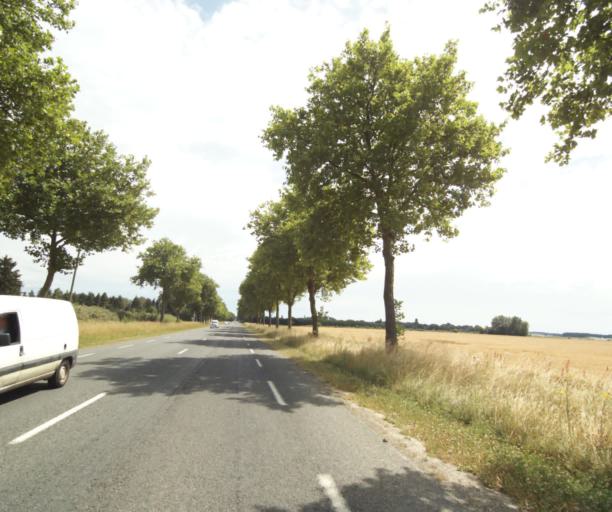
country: FR
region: Ile-de-France
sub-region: Departement de Seine-et-Marne
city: Chailly-en-Biere
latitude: 48.4769
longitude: 2.5983
